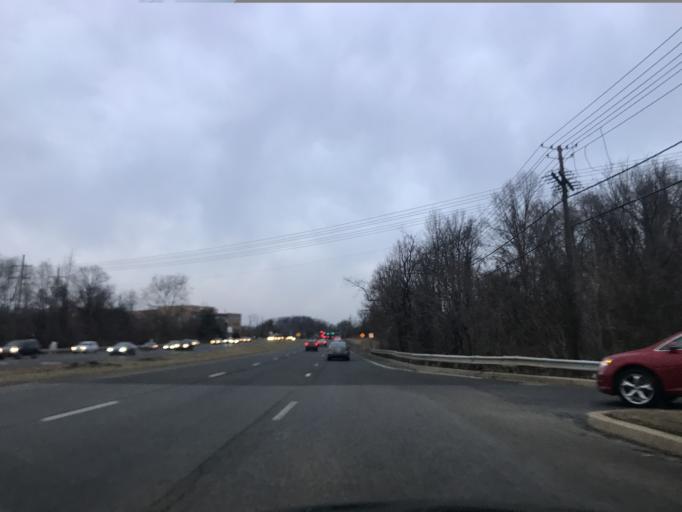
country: US
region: Maryland
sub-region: Prince George's County
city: Lake Arbor
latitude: 38.9037
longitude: -76.8333
